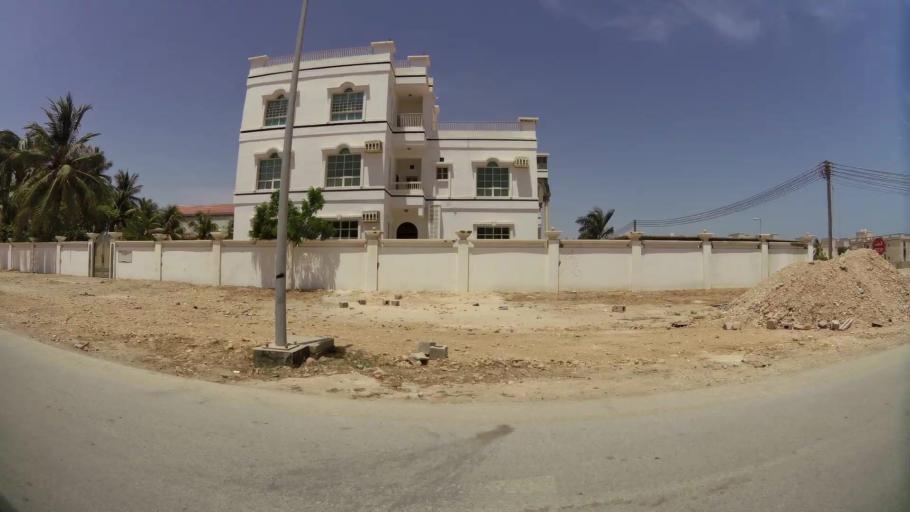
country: OM
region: Zufar
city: Salalah
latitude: 17.0615
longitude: 54.1512
